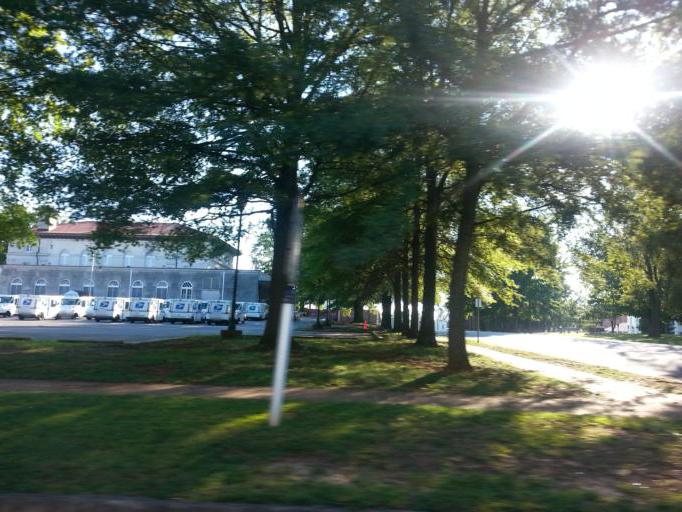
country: US
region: Alabama
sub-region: Lauderdale County
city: Florence
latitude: 34.8030
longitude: -87.6744
